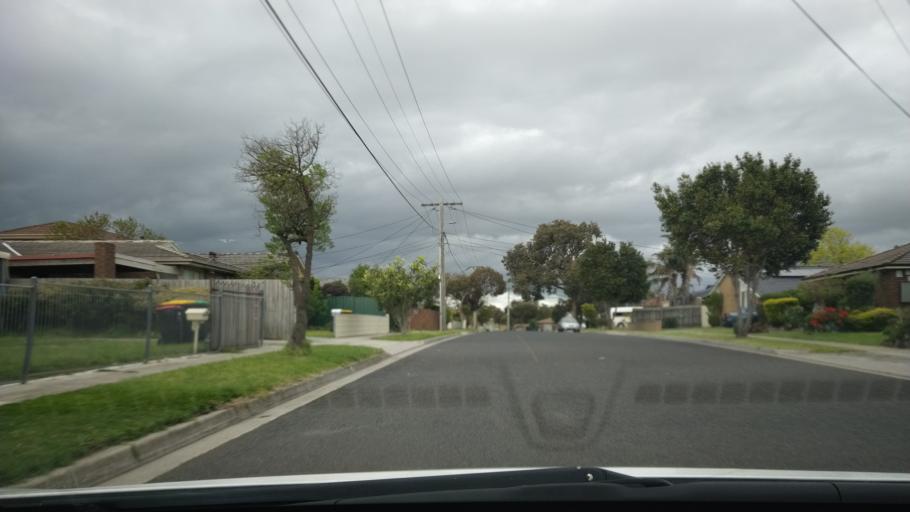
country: AU
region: Victoria
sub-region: Greater Dandenong
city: Keysborough
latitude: -37.9835
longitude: 145.1599
